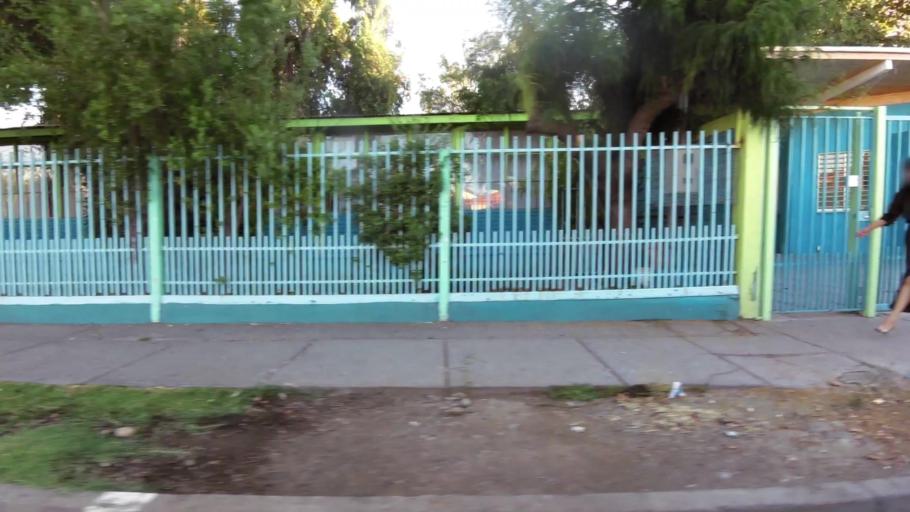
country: CL
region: O'Higgins
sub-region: Provincia de Cachapoal
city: Rancagua
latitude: -34.1718
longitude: -70.7590
